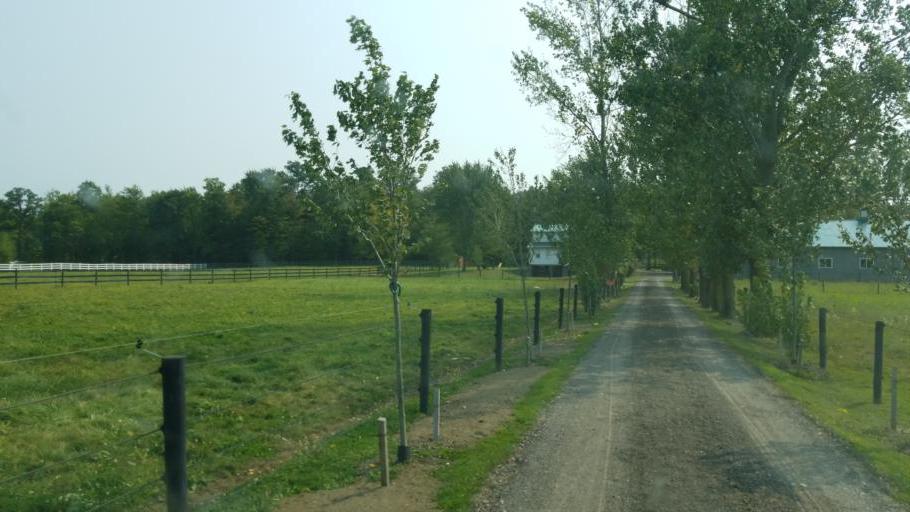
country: US
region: Ohio
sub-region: Geauga County
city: Middlefield
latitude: 41.4936
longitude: -81.0243
